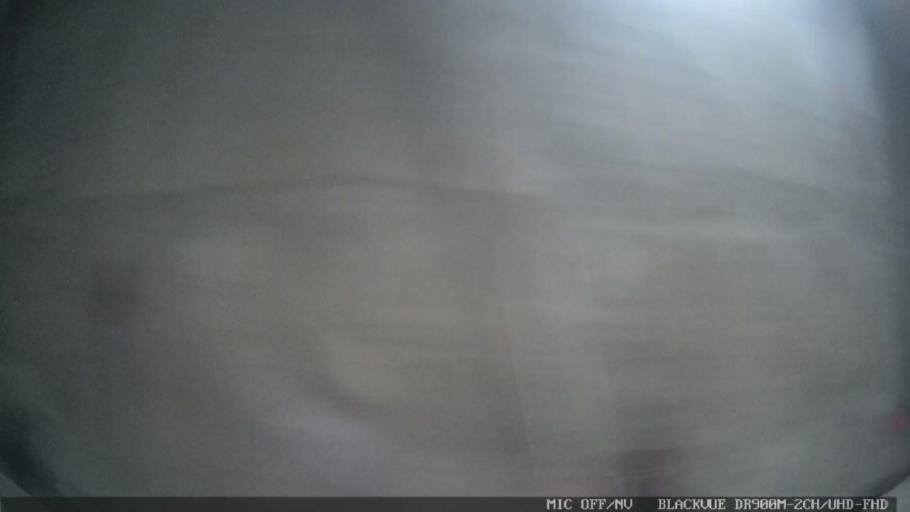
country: BR
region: Sao Paulo
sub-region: Cubatao
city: Cubatao
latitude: -23.9161
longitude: -46.5290
